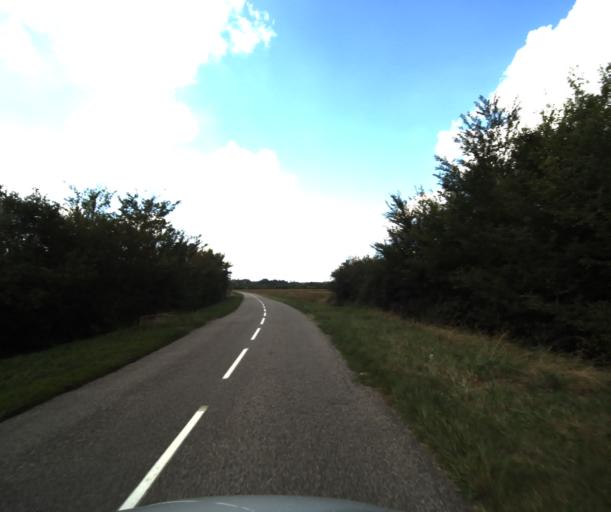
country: FR
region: Midi-Pyrenees
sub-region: Departement de la Haute-Garonne
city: Lherm
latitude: 43.4274
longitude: 1.2432
